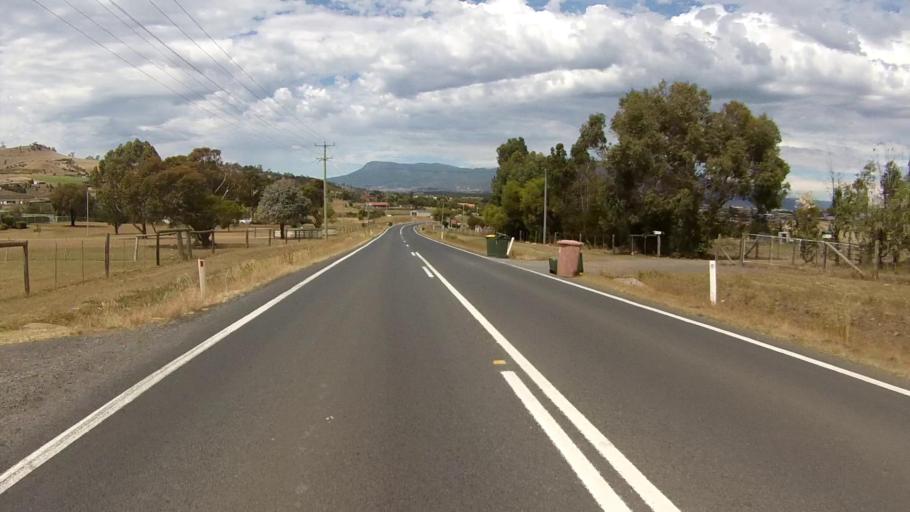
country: AU
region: Tasmania
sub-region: Brighton
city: Bridgewater
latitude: -42.6978
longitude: 147.2694
